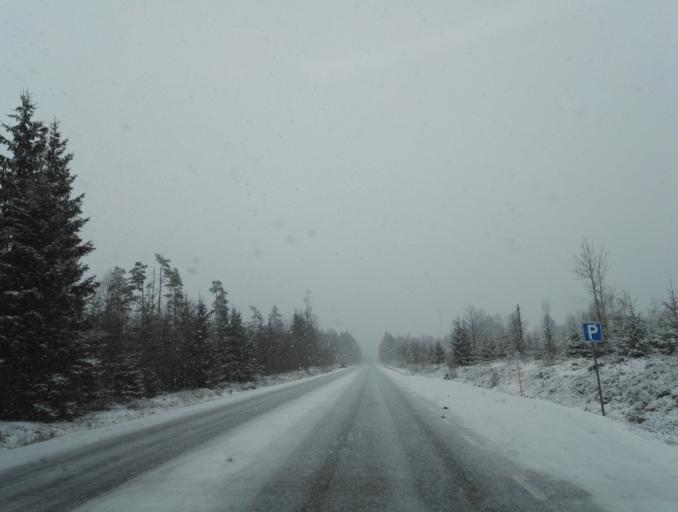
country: SE
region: Kronoberg
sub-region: Uppvidinge Kommun
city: Lenhovda
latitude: 57.0369
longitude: 15.2155
